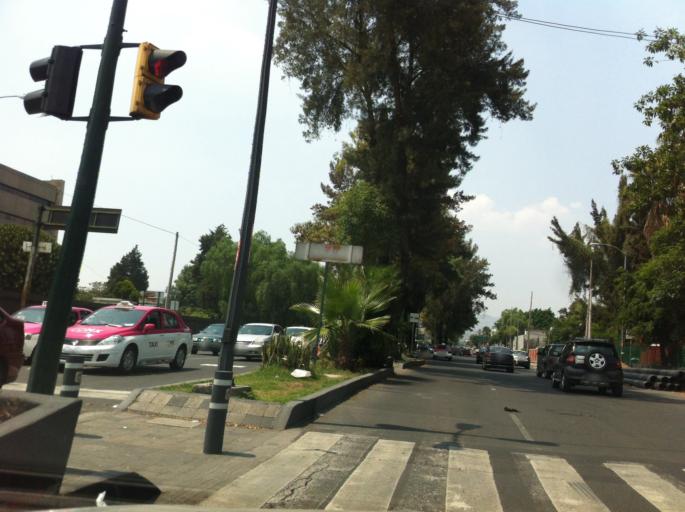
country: MX
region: Mexico
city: Colonia Lindavista
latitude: 19.4847
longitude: -99.1347
